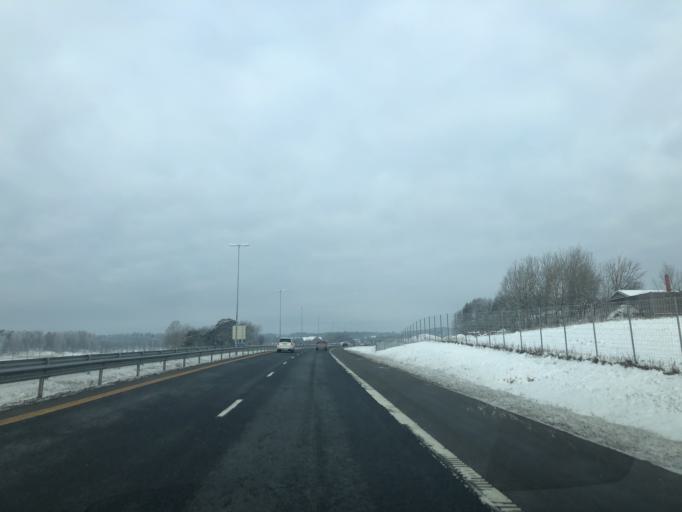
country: NO
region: Ostfold
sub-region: Sarpsborg
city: Skjeberg
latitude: 59.1386
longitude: 11.2587
